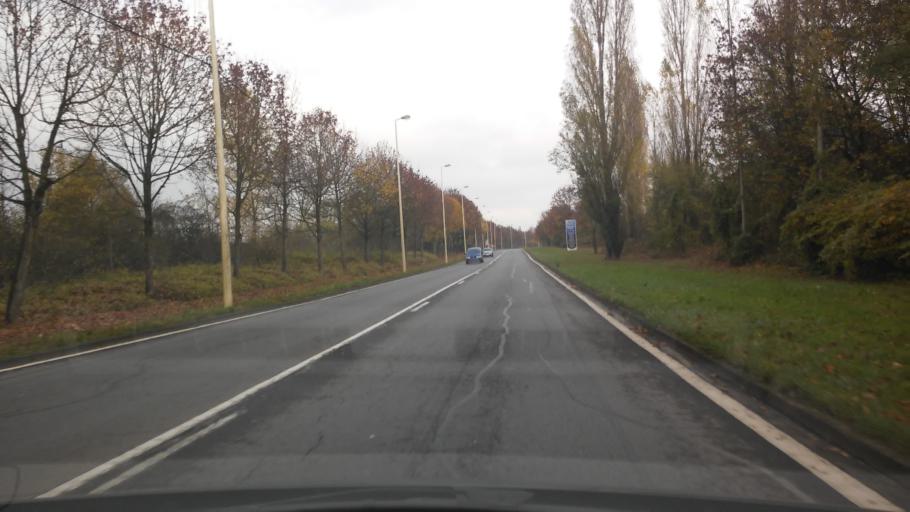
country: FR
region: Lorraine
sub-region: Departement de la Moselle
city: Terville
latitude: 49.3318
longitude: 6.1532
